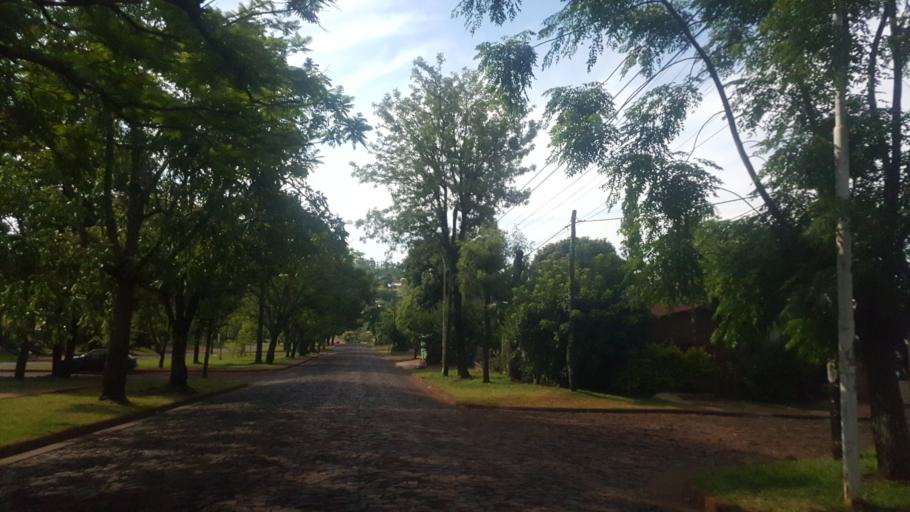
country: AR
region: Misiones
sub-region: Departamento de Leandro N. Alem
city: Leandro N. Alem
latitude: -27.5991
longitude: -55.3308
